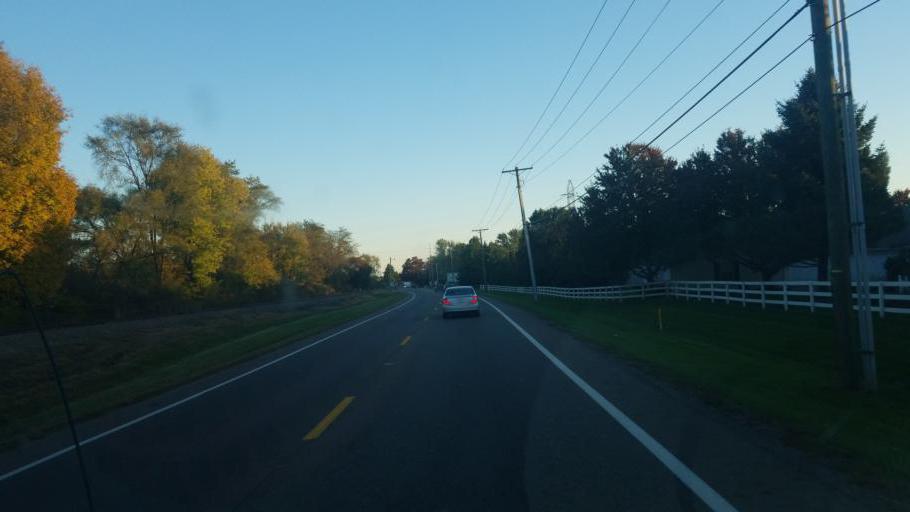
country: US
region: Ohio
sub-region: Licking County
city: Newark
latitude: 40.0946
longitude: -82.4220
